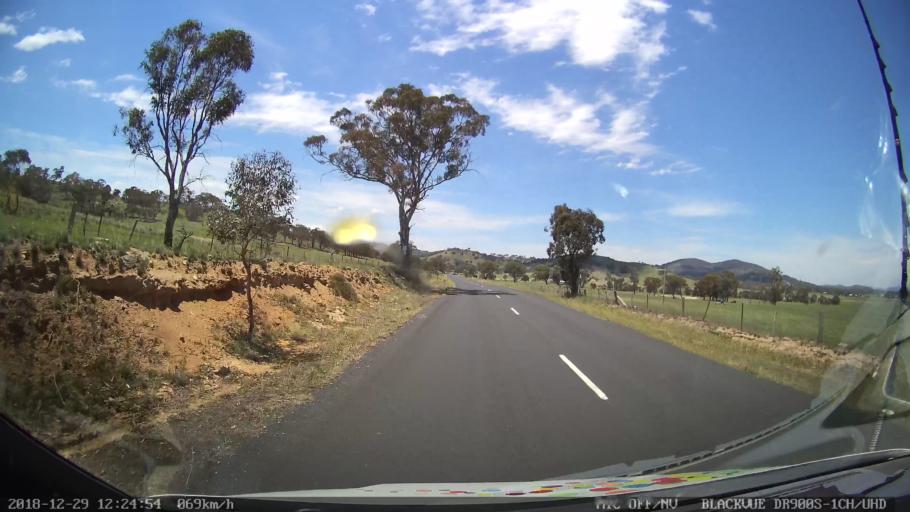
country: AU
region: Australian Capital Territory
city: Macarthur
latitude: -35.4510
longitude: 149.2104
